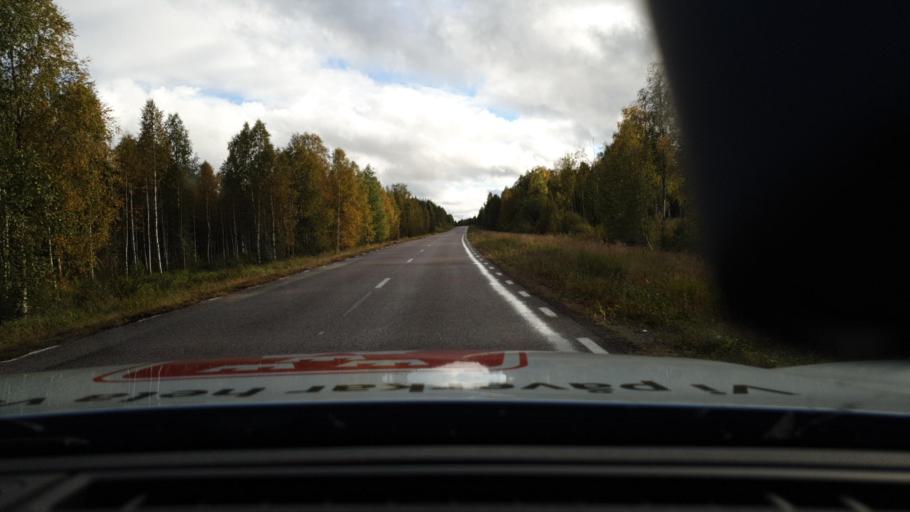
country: SE
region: Norrbotten
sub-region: Overkalix Kommun
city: OEverkalix
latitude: 66.8471
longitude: 22.7586
